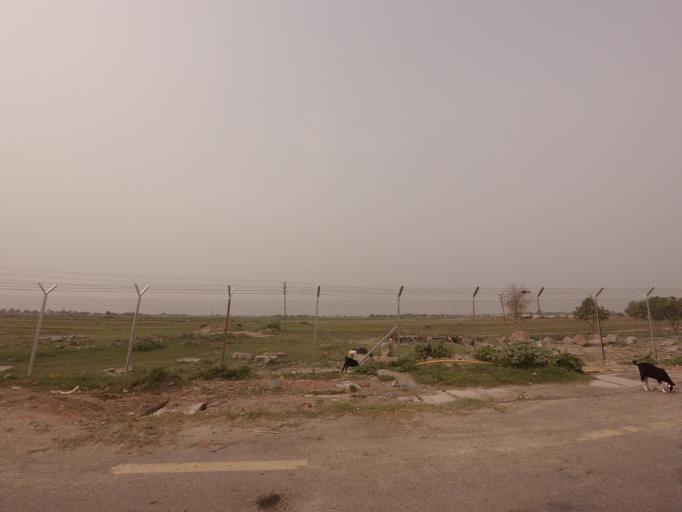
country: NP
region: Western Region
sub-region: Lumbini Zone
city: Bhairahawa
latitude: 27.5119
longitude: 83.4034
